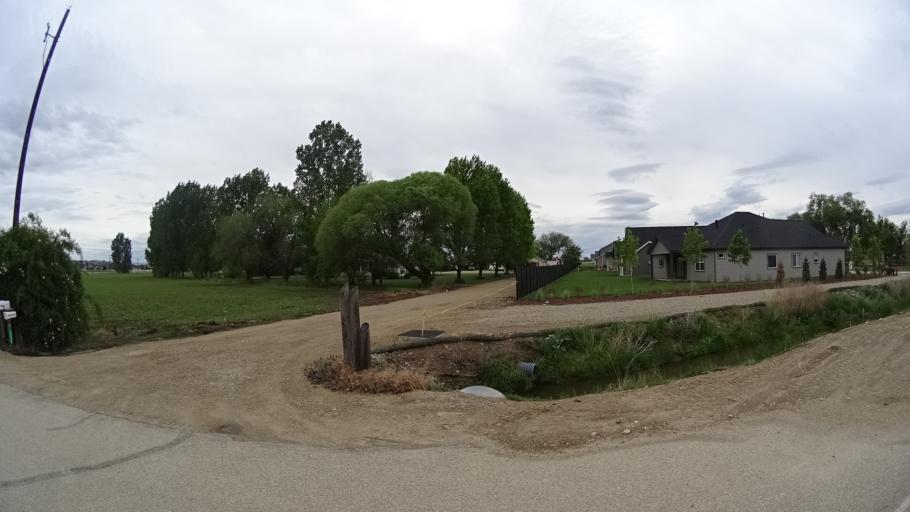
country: US
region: Idaho
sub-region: Ada County
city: Star
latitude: 43.7160
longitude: -116.5031
